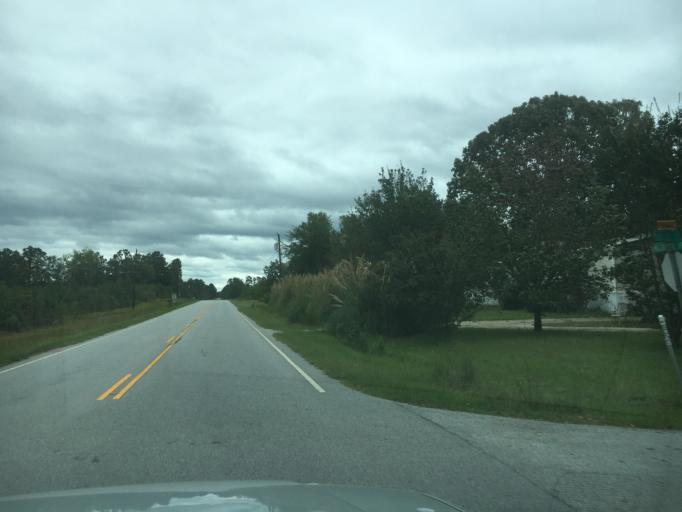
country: US
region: South Carolina
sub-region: Greenwood County
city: Greenwood
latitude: 34.1191
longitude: -82.2490
